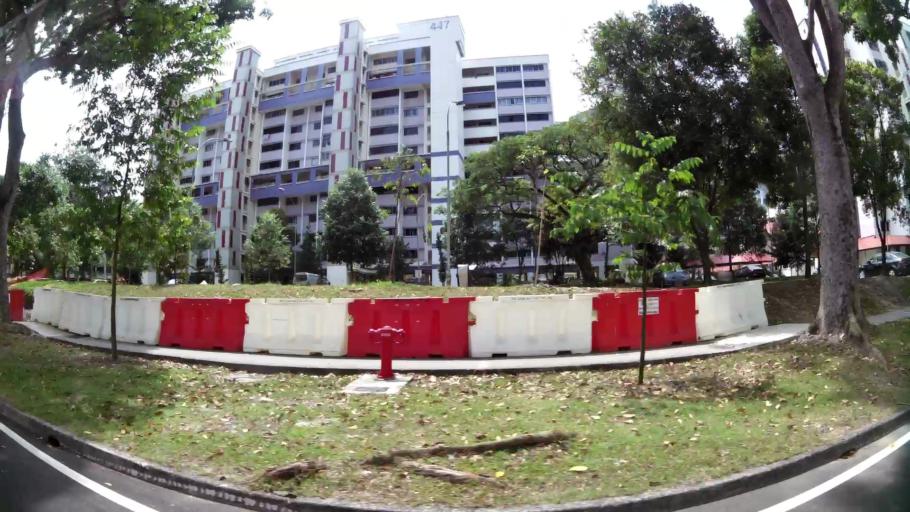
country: MY
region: Johor
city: Johor Bahru
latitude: 1.3530
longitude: 103.7202
